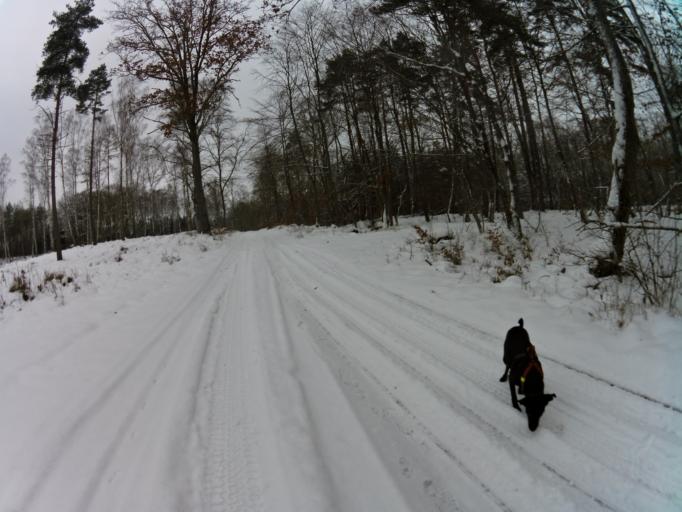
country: PL
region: West Pomeranian Voivodeship
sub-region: Powiat stargardzki
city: Dobrzany
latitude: 53.3463
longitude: 15.5152
